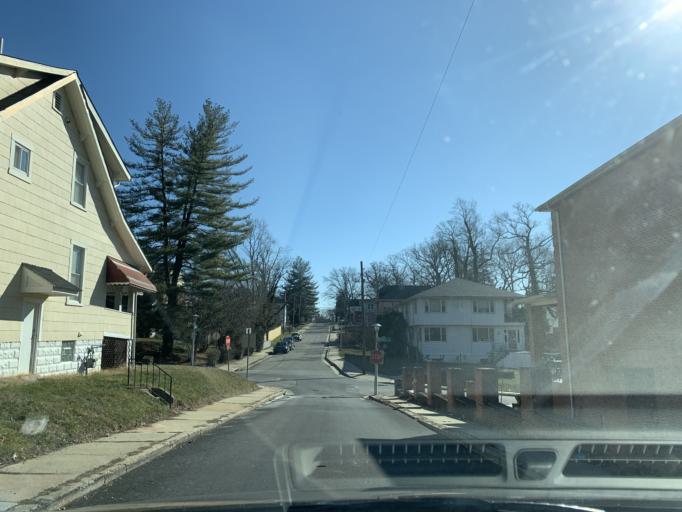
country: US
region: Maryland
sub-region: Baltimore County
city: Lochearn
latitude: 39.3192
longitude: -76.6860
